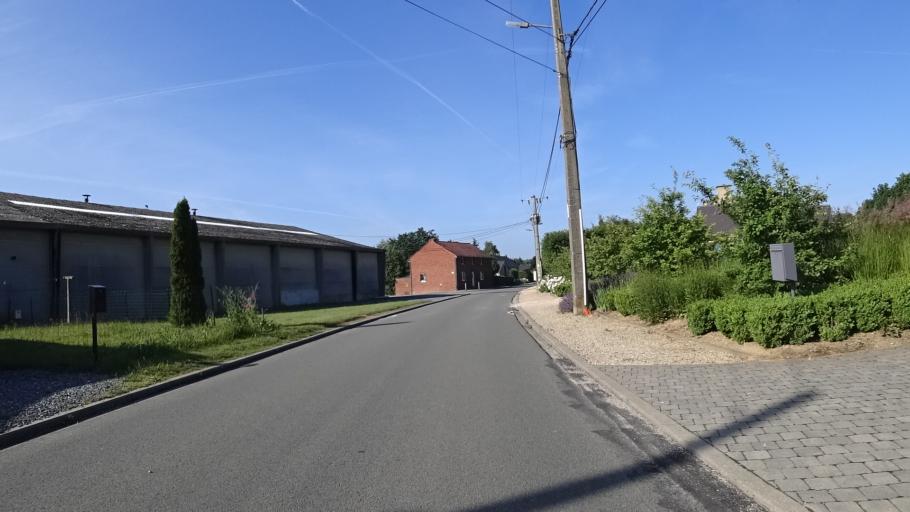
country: BE
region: Wallonia
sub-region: Province du Brabant Wallon
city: Perwez
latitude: 50.5545
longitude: 4.7949
